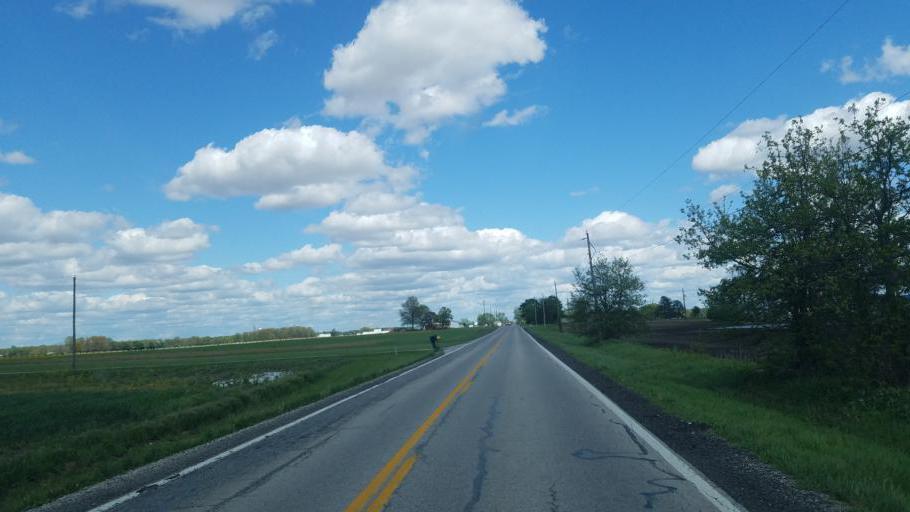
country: US
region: Ohio
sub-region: Marion County
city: Prospect
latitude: 40.4515
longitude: -83.1155
